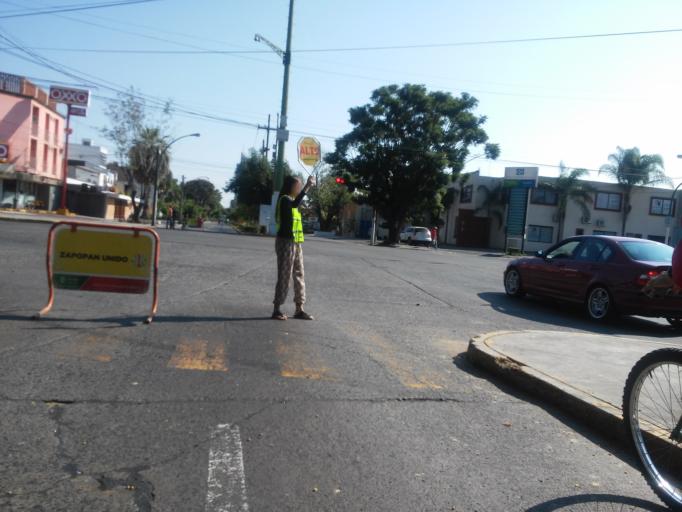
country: MX
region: Jalisco
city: Guadalajara
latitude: 20.6613
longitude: -103.4072
